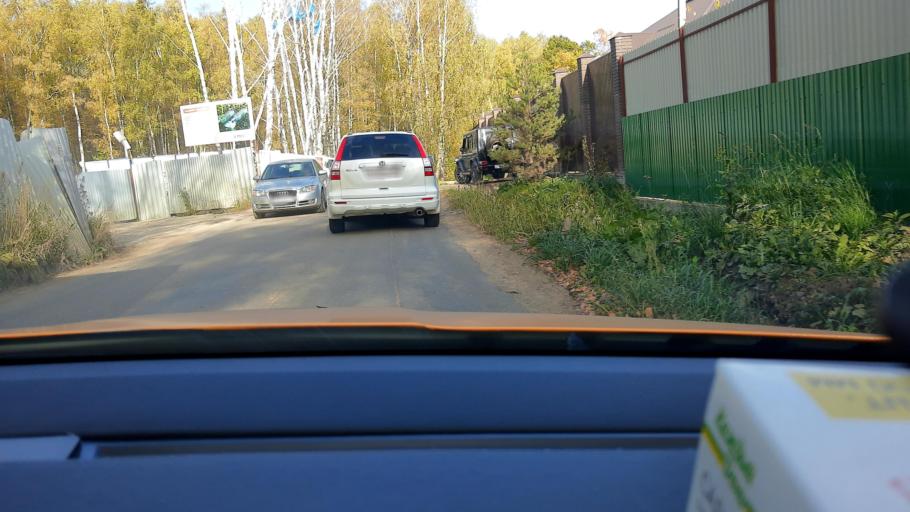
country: RU
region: Moskovskaya
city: Gorki-Leninskiye
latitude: 55.5251
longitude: 37.8009
